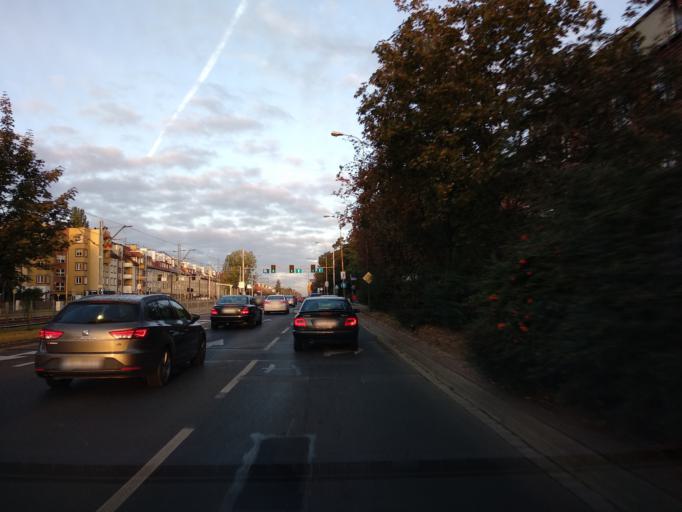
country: PL
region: Lower Silesian Voivodeship
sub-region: Powiat wroclawski
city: Wroclaw
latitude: 51.0903
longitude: 16.9944
